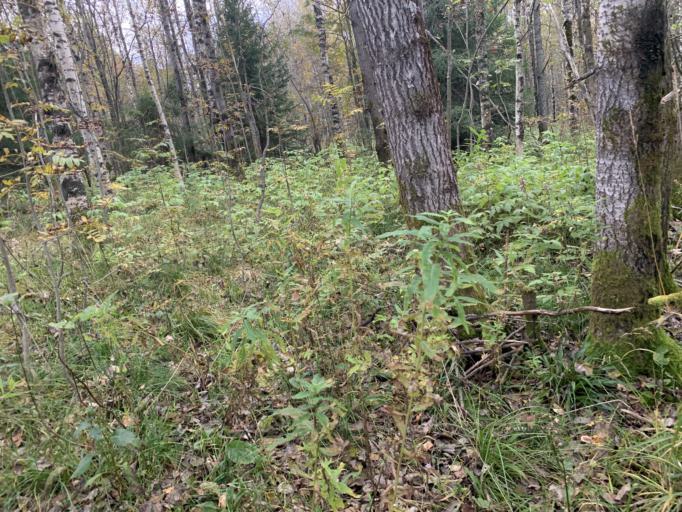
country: RU
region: Perm
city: Gubakha
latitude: 58.8465
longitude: 57.5800
